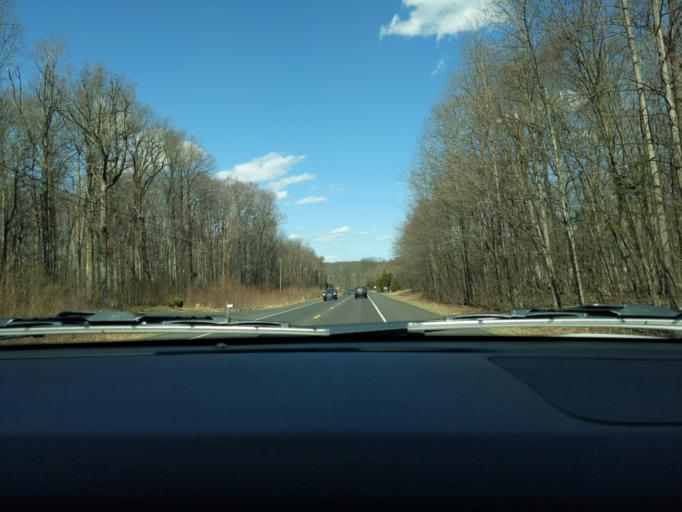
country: US
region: Pennsylvania
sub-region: Bucks County
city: Perkasie
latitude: 40.4290
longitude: -75.2699
